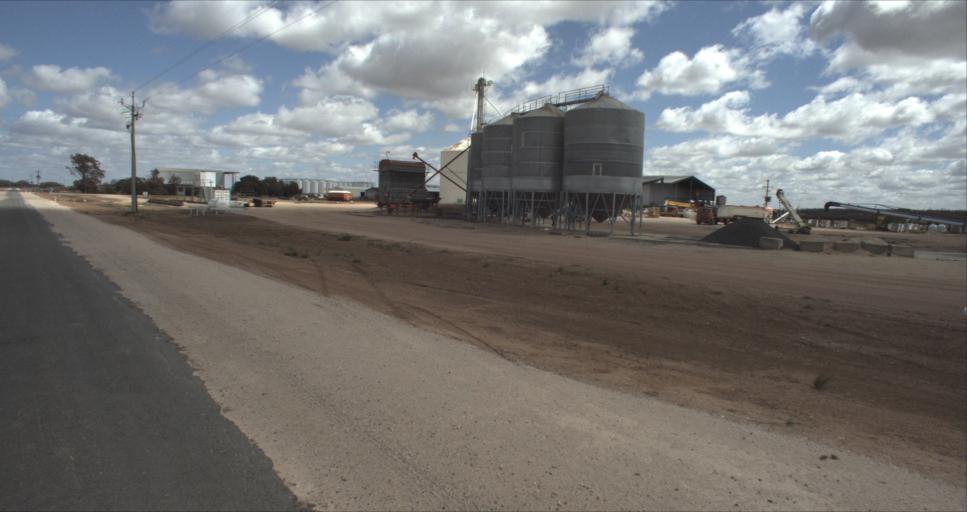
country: AU
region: New South Wales
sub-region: Murrumbidgee Shire
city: Darlington Point
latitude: -34.5764
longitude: 146.1804
